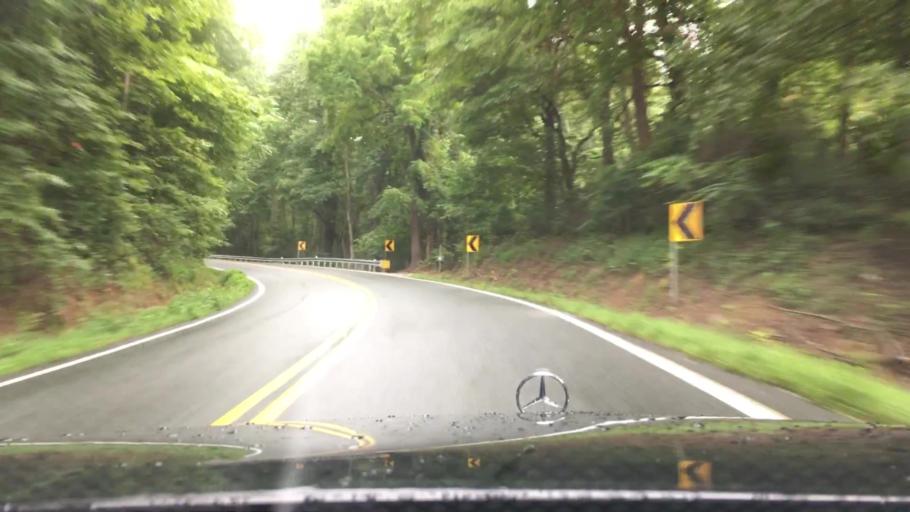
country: US
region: Virginia
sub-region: Nelson County
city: Nellysford
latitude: 37.8625
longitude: -78.9210
